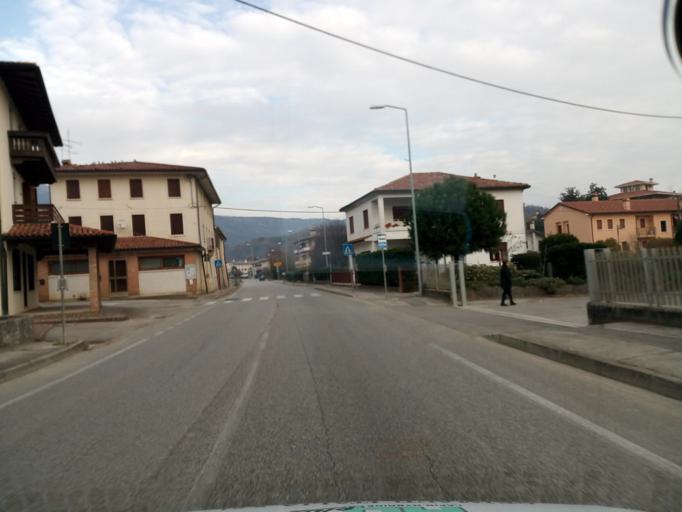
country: IT
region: Veneto
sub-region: Provincia di Treviso
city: Castelcucco
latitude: 45.8267
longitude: 11.8856
